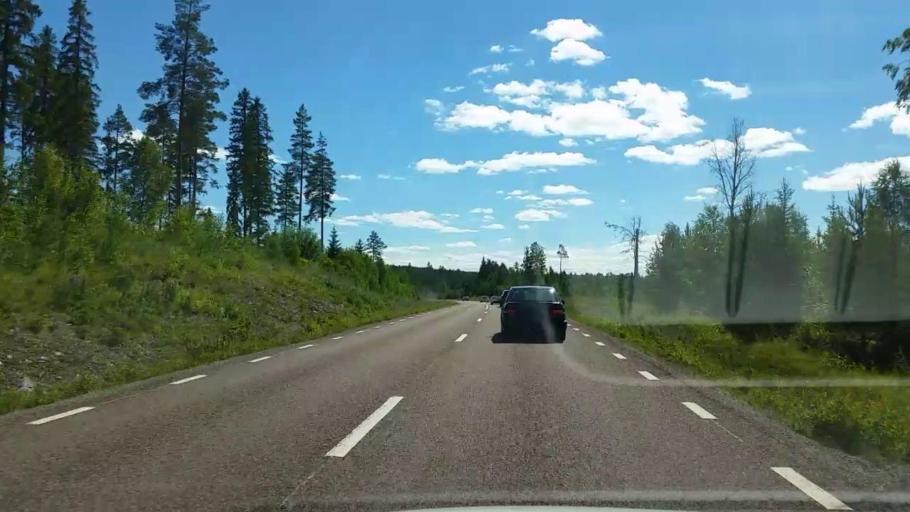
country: SE
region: Gaevleborg
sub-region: Ovanakers Kommun
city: Edsbyn
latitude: 61.2403
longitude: 15.8819
